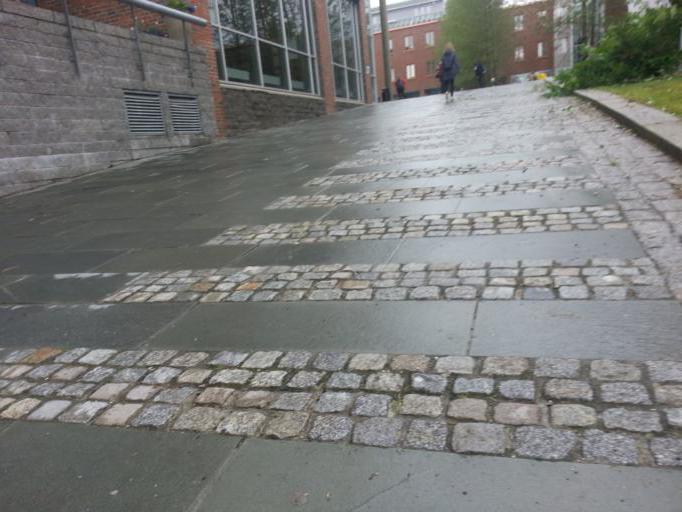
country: NO
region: Troms
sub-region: Tromso
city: Tromso
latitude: 69.6820
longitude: 18.9768
